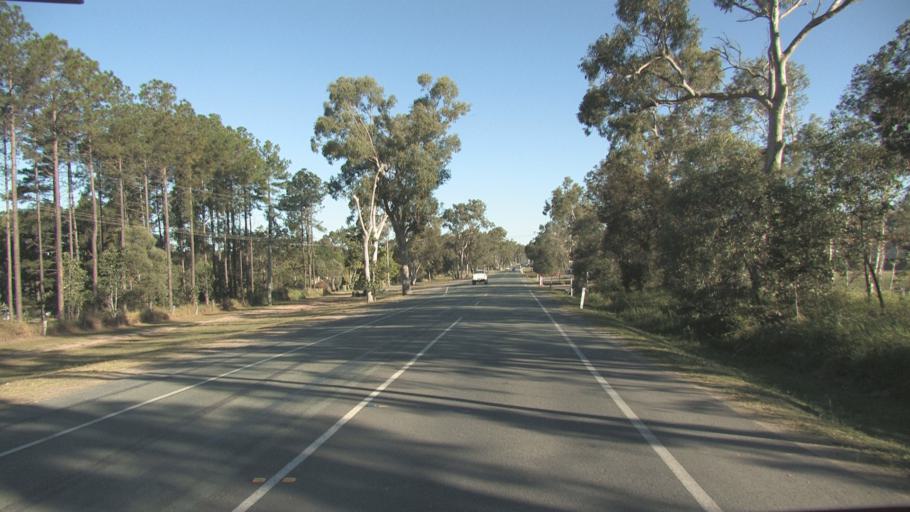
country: AU
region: Queensland
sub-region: Logan
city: Logan Reserve
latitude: -27.7123
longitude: 153.0932
